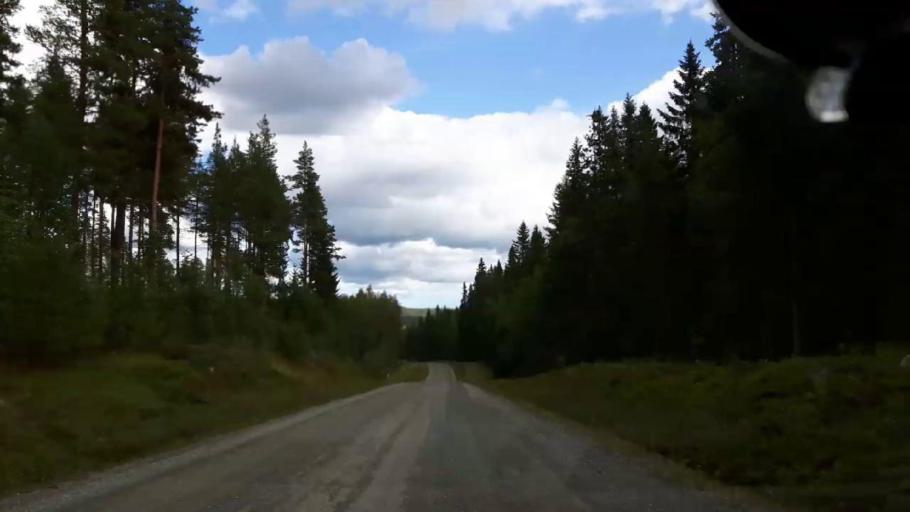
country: SE
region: Jaemtland
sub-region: Stroemsunds Kommun
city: Stroemsund
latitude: 63.3951
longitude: 15.7177
